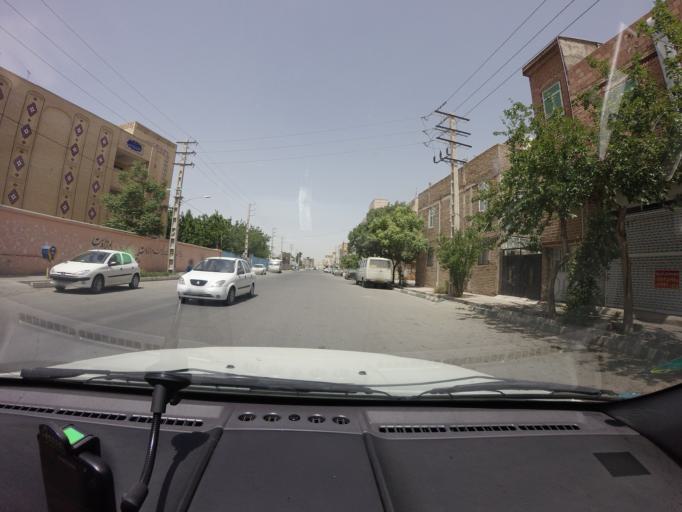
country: IR
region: Tehran
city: Eslamshahr
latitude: 35.5279
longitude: 51.2165
